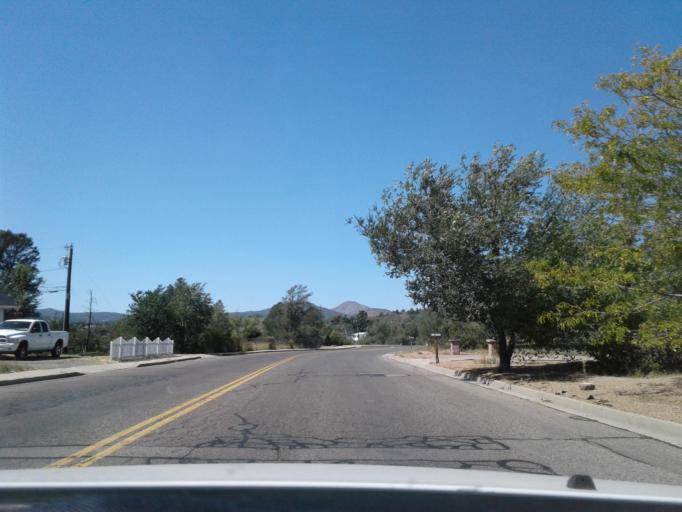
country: US
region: Arizona
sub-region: Yavapai County
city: Prescott
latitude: 34.5697
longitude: -112.4716
